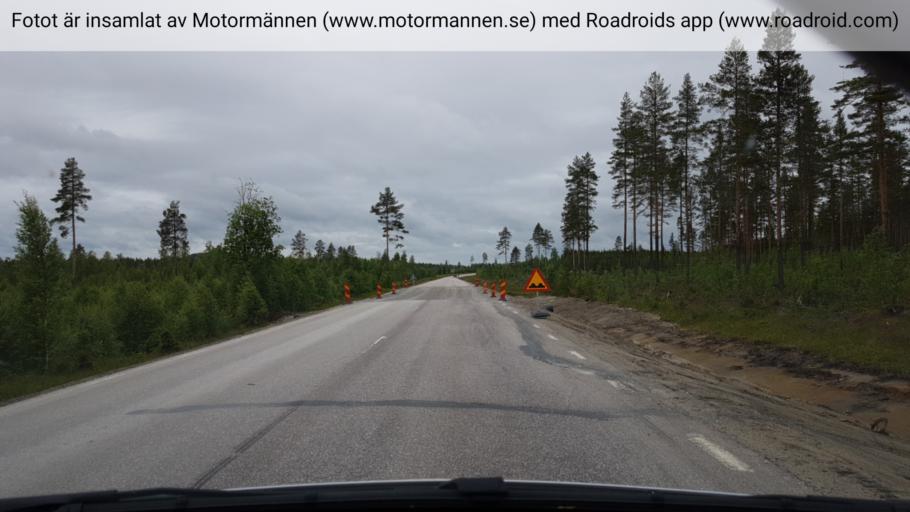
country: SE
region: Vaesterbotten
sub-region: Vindelns Kommun
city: Vindeln
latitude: 64.0584
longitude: 19.6472
